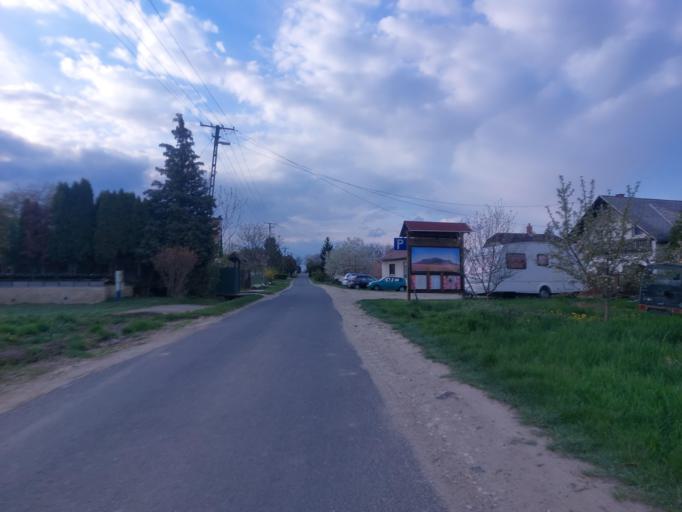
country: HU
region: Veszprem
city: Devecser
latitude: 47.1543
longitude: 17.3798
